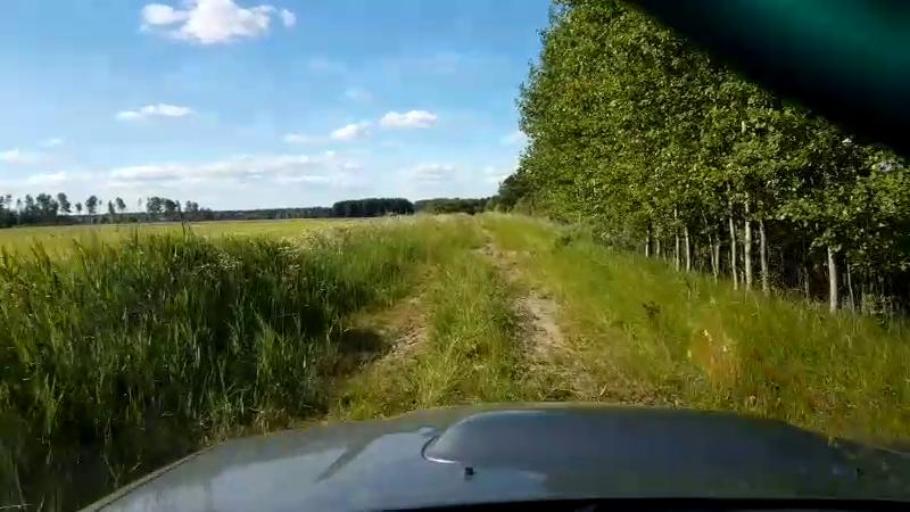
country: EE
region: Paernumaa
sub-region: Sauga vald
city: Sauga
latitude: 58.5021
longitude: 24.5908
